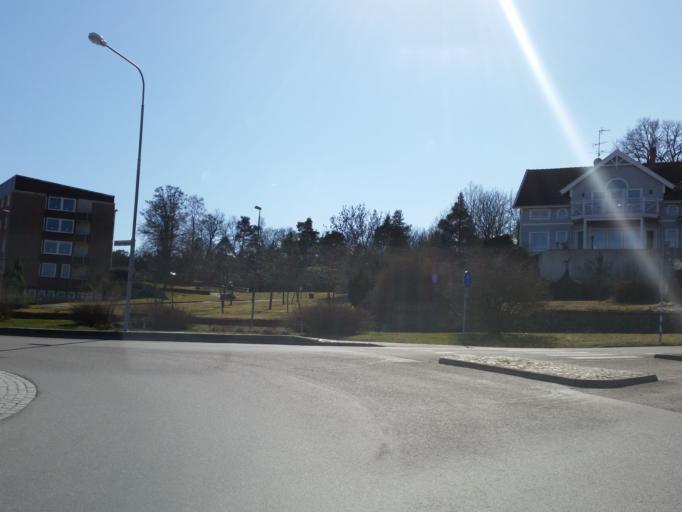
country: SE
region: Kalmar
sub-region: Oskarshamns Kommun
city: Oskarshamn
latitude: 57.2632
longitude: 16.4567
